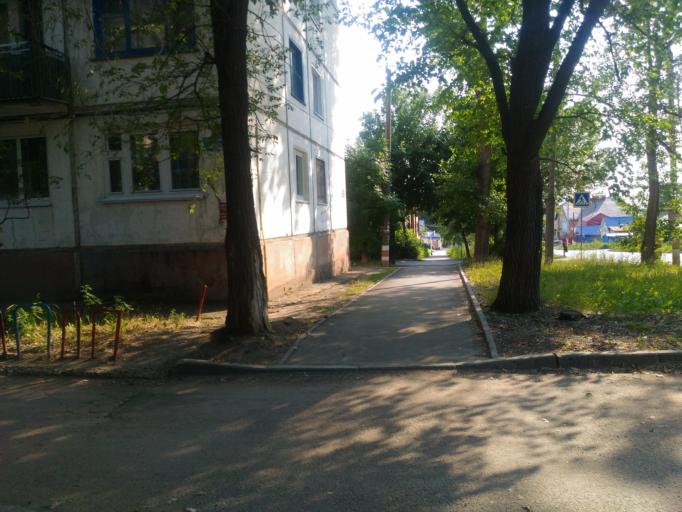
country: RU
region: Ulyanovsk
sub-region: Ulyanovskiy Rayon
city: Ulyanovsk
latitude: 54.3408
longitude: 48.3678
